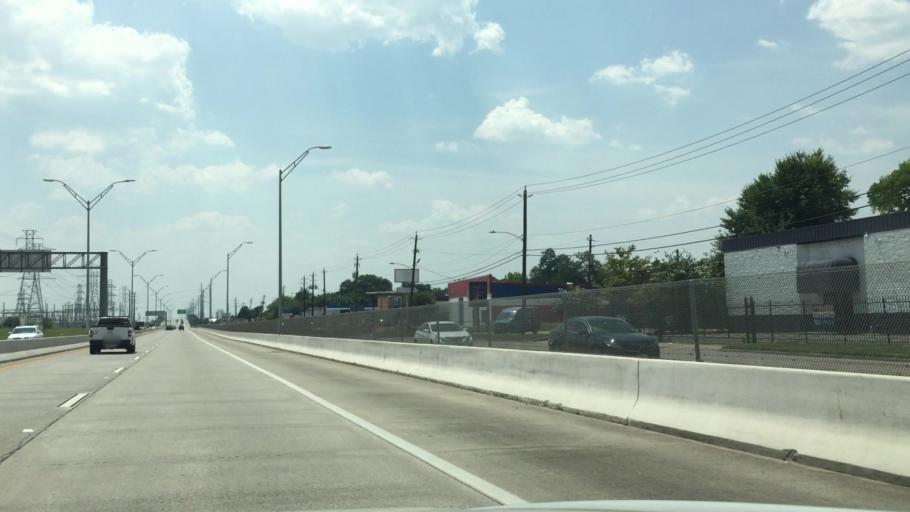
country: US
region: Texas
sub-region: Harris County
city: Piney Point Village
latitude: 29.7208
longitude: -95.5265
